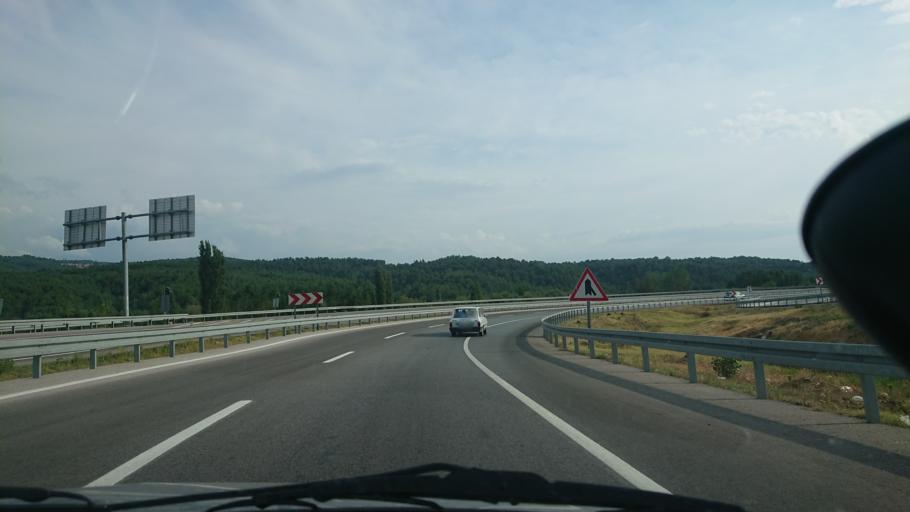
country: TR
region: Kuetahya
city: Gediz
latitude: 38.9339
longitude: 29.3112
